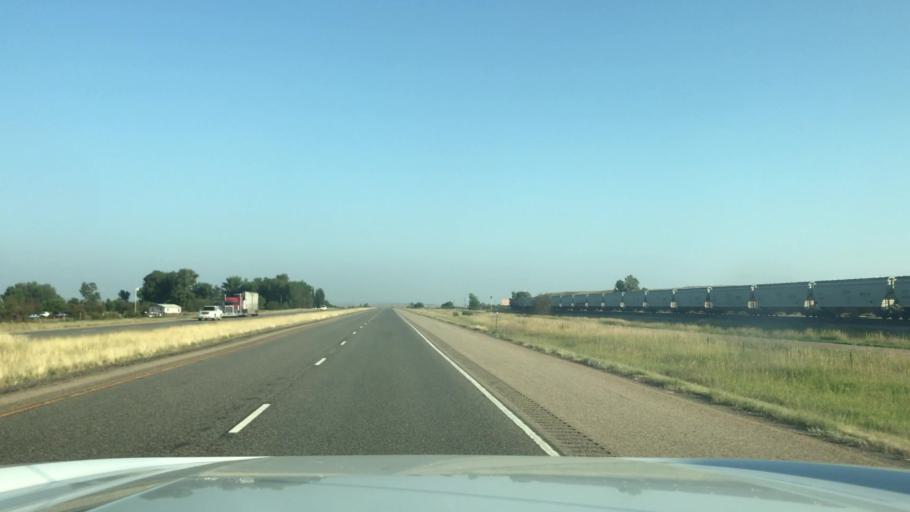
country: US
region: Montana
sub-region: Big Horn County
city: Crow Agency
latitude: 45.6560
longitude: -107.4827
